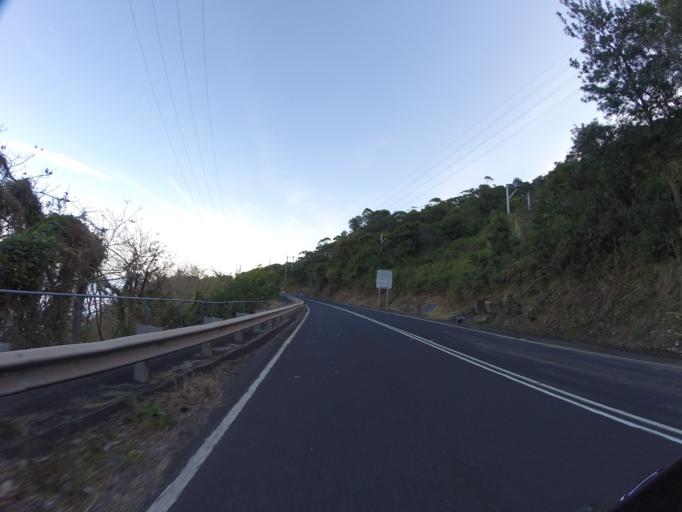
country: AU
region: New South Wales
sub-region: Wollongong
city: Helensburgh
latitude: -34.2617
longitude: 150.9671
